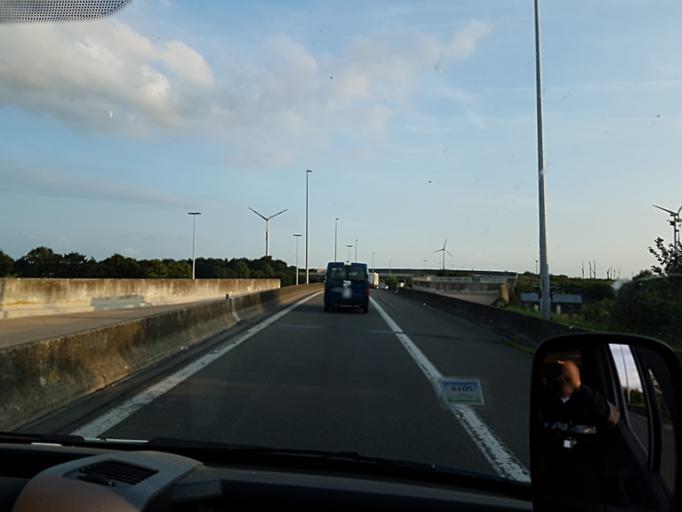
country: BE
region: Flanders
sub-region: Provincie Antwerpen
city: Hoogstraten
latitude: 51.4161
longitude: 4.7029
